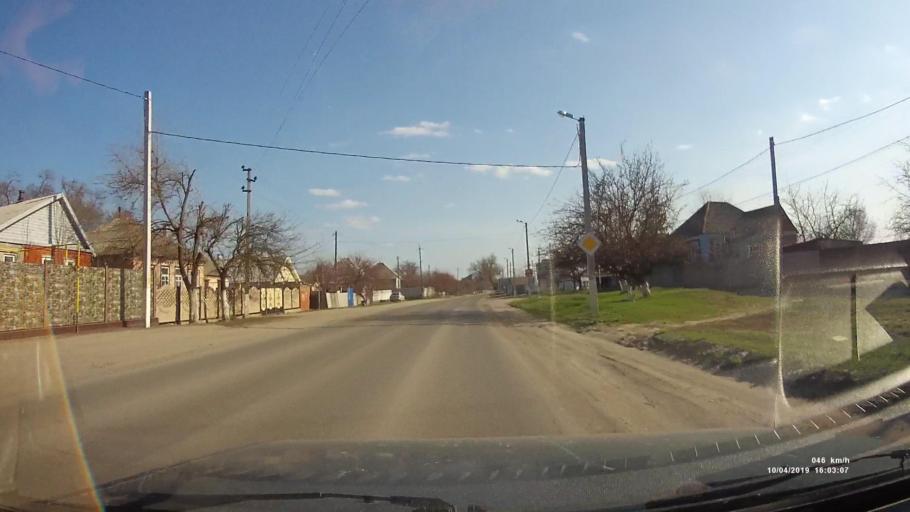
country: RU
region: Rostov
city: Masalovka
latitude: 48.3650
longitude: 40.2645
